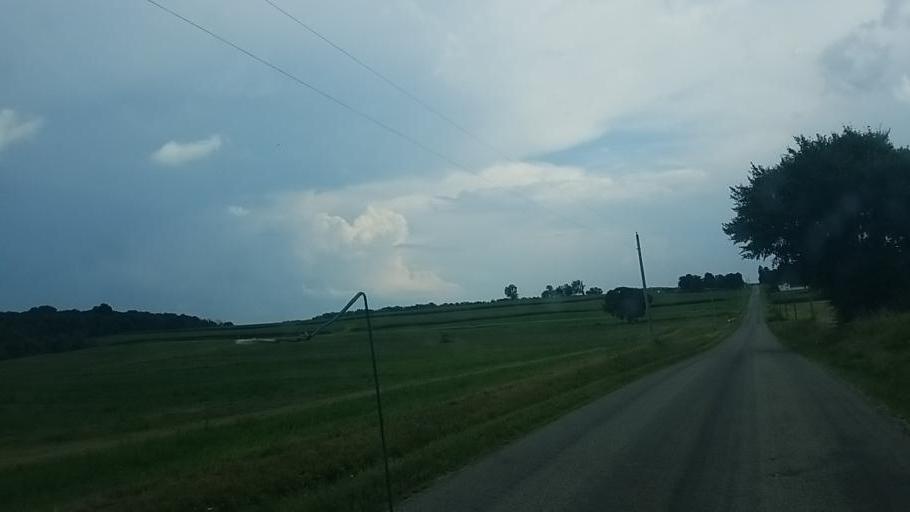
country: US
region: Ohio
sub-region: Wayne County
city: Creston
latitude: 40.9776
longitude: -81.9385
